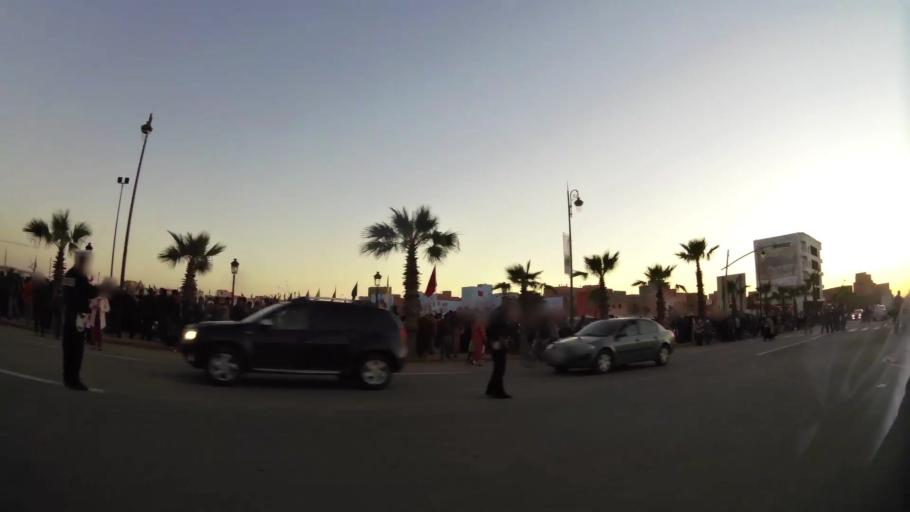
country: MA
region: Marrakech-Tensift-Al Haouz
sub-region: Kelaa-Des-Sraghna
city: Sidi Bou Othmane
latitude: 32.2272
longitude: -7.9452
